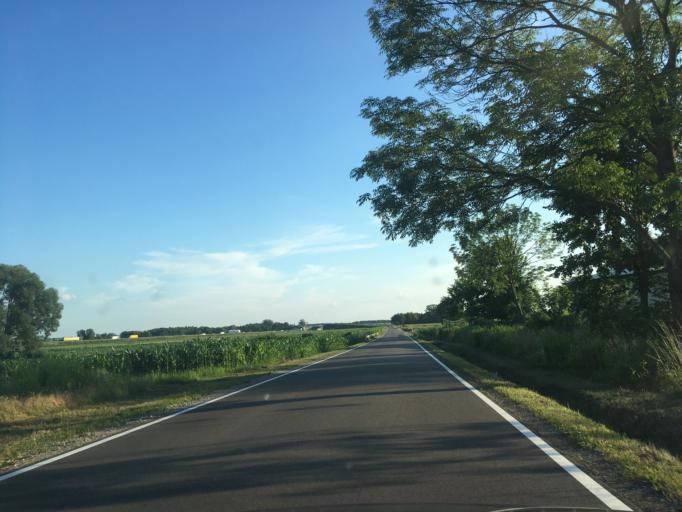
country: PL
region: Masovian Voivodeship
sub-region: Powiat warszawski zachodni
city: Blonie
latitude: 52.1488
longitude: 20.6028
